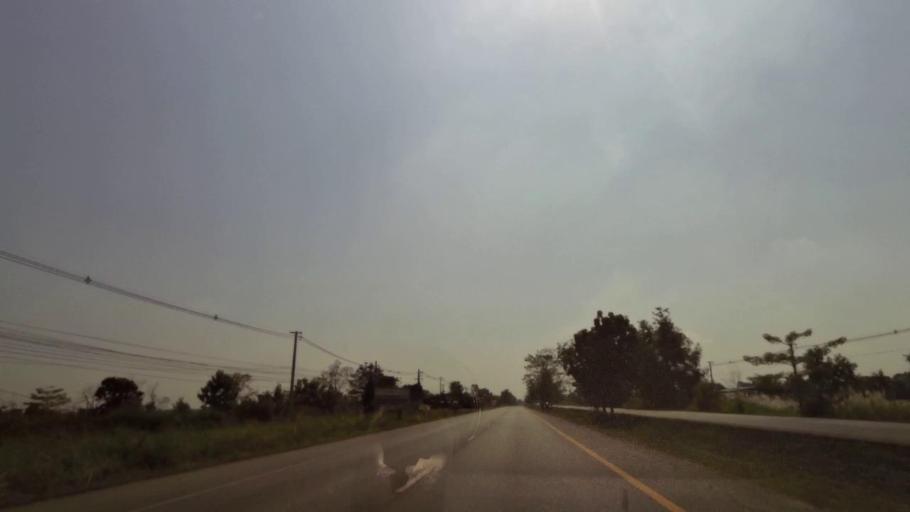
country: TH
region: Phichit
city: Bueng Na Rang
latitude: 16.3061
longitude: 100.1286
